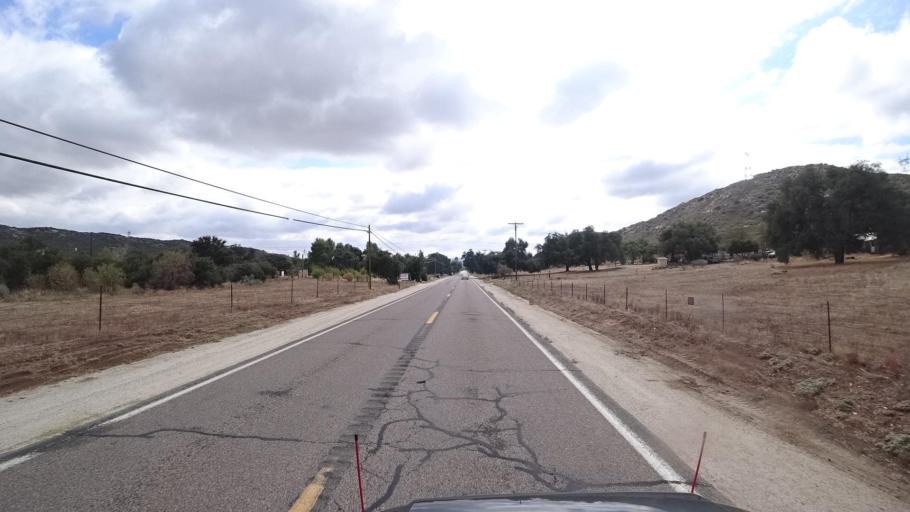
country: US
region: California
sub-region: San Diego County
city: Campo
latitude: 32.6661
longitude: -116.4882
